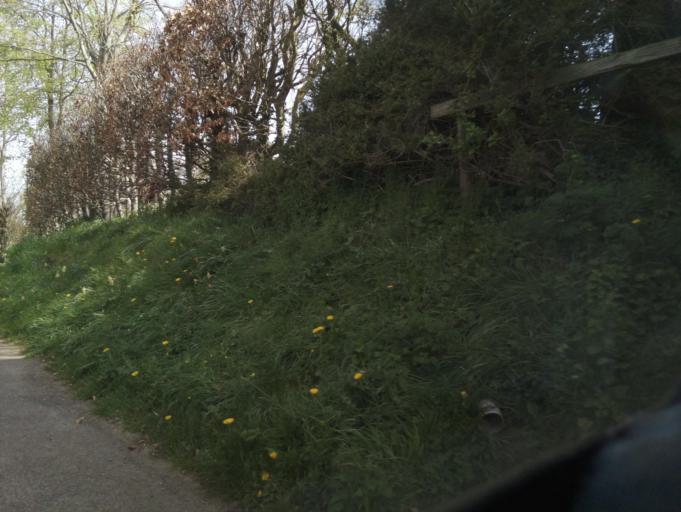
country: GB
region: England
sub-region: Dorset
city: Sherborne
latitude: 50.9789
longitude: -2.5335
